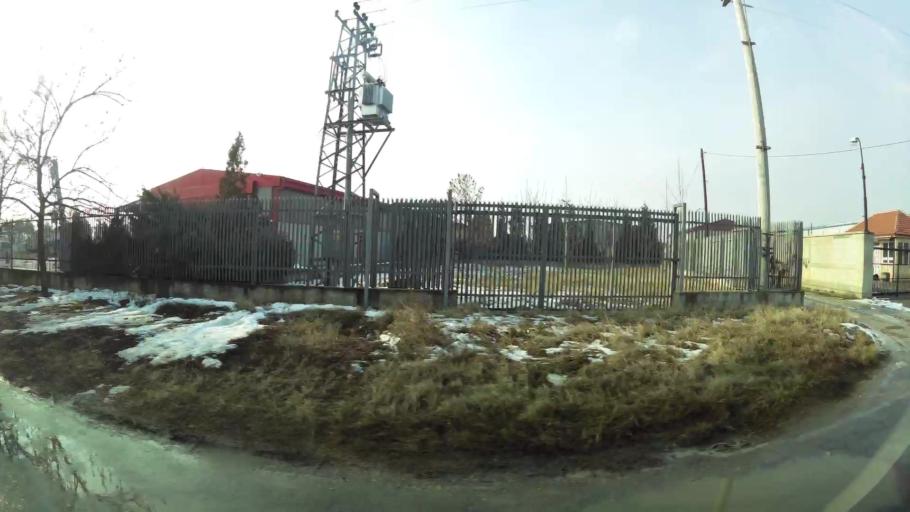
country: MK
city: Kadino
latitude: 41.9756
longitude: 21.5983
